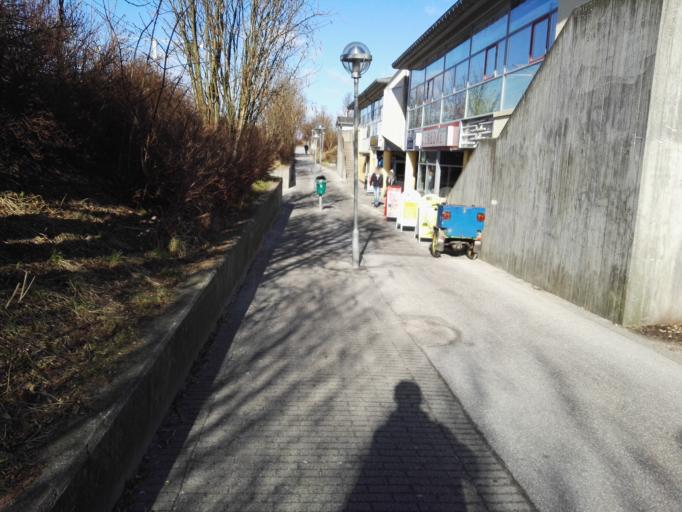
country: DK
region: Capital Region
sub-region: Egedal Kommune
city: Stenlose
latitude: 55.7675
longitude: 12.1901
